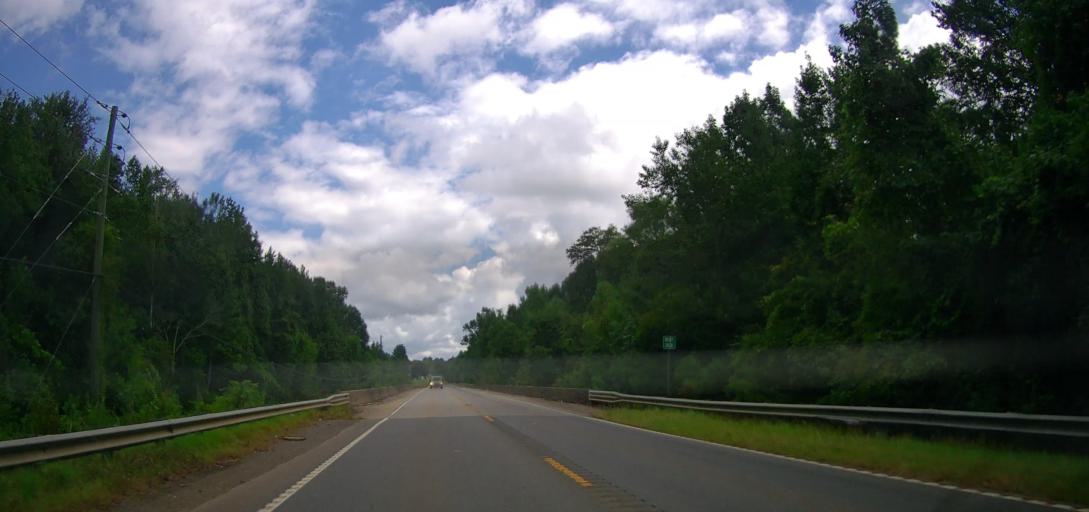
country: US
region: Georgia
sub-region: Houston County
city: Perry
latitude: 32.4504
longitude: -83.6243
